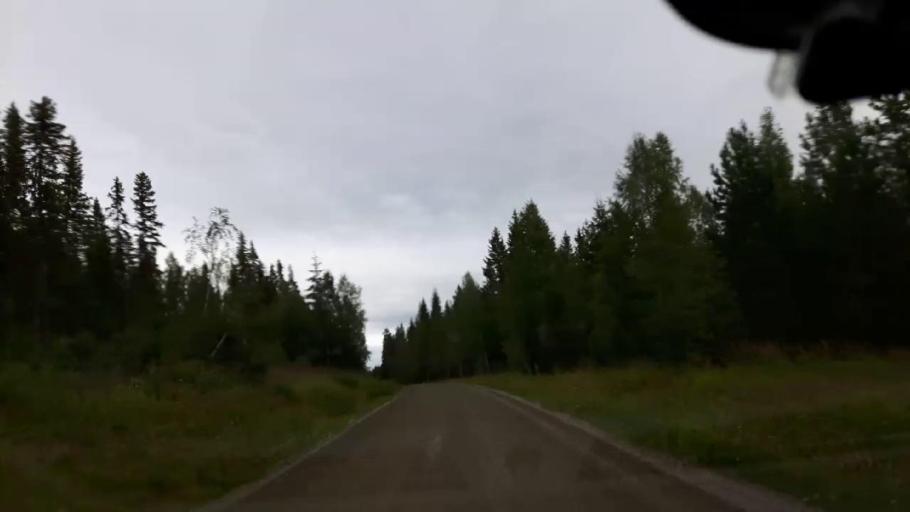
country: SE
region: Jaemtland
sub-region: Braecke Kommun
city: Braecke
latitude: 62.9293
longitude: 15.4989
